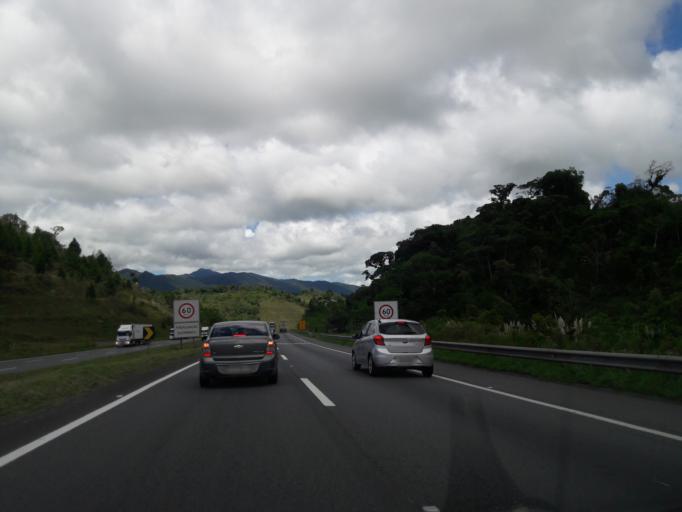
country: BR
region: Parana
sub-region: Antonina
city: Antonina
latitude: -25.0121
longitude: -48.5083
